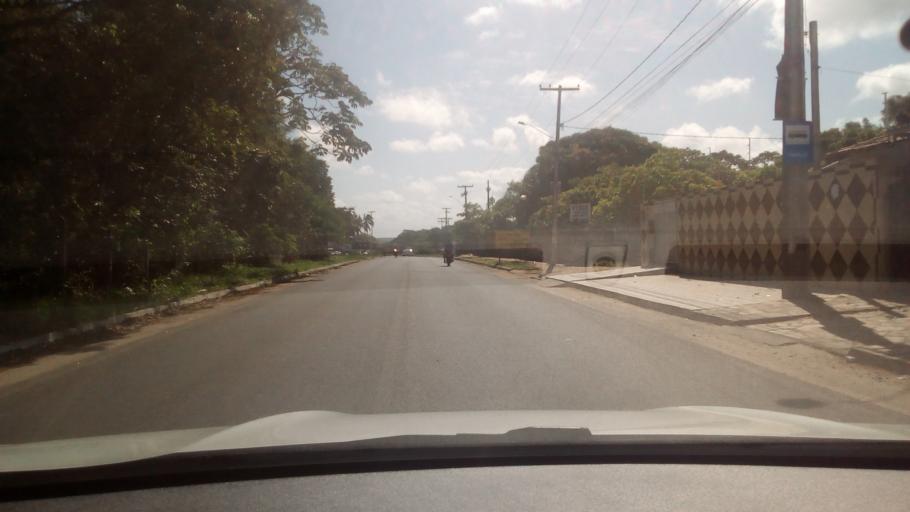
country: BR
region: Paraiba
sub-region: Conde
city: Conde
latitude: -7.2172
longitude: -34.8335
